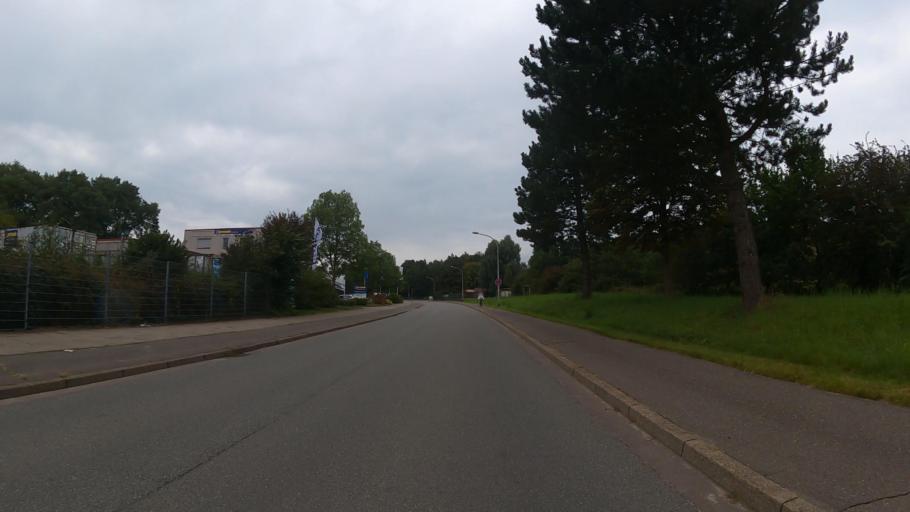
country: DE
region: Schleswig-Holstein
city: Pinneberg
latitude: 53.6635
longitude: 9.7848
